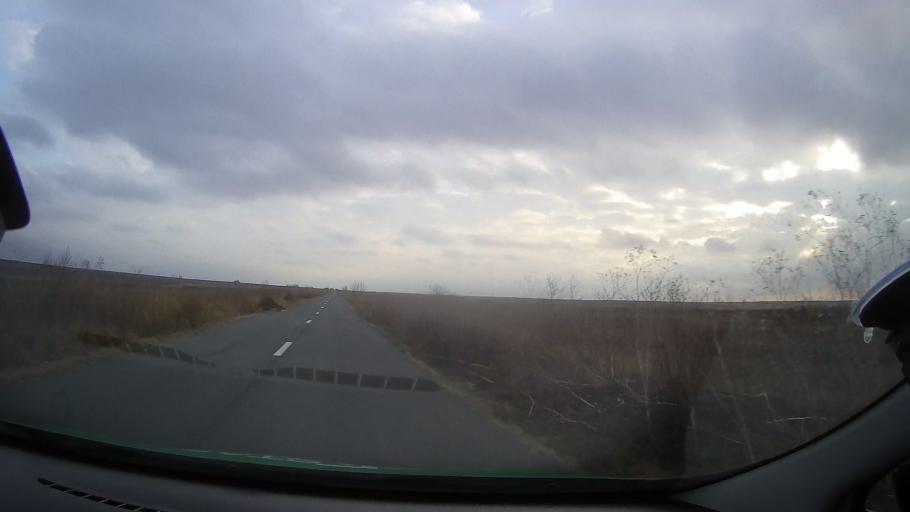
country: RO
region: Constanta
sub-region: Comuna Pestera
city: Pestera
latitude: 44.1494
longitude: 28.1143
